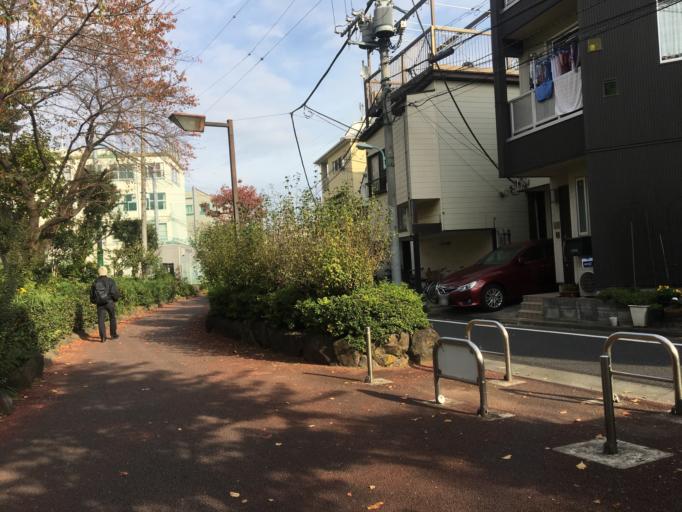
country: JP
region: Tokyo
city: Tokyo
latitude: 35.6087
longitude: 139.6797
